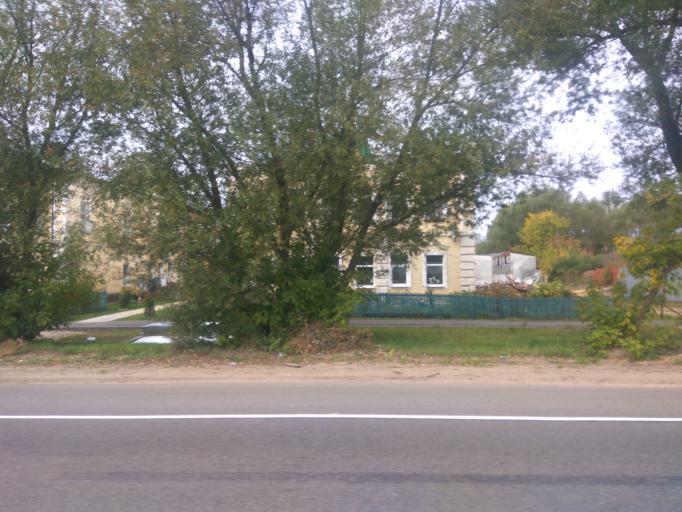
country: RU
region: Moskovskaya
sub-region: Shchelkovskiy Rayon
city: Grebnevo
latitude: 55.9879
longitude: 38.1255
